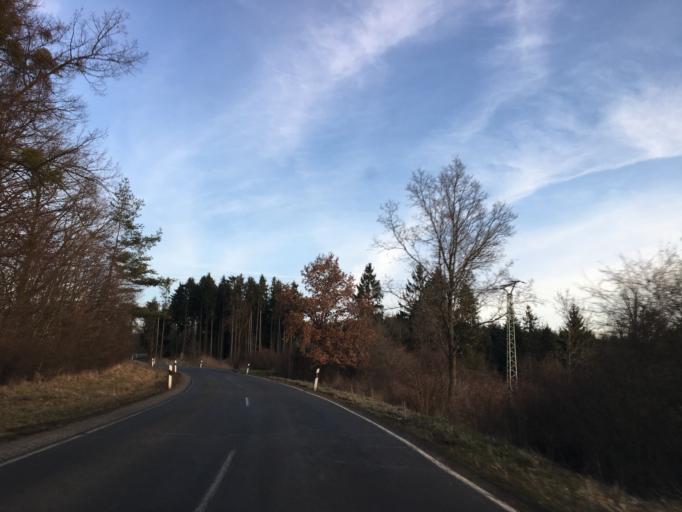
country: DE
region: Hesse
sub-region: Regierungsbezirk Giessen
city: Lauterbach
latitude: 50.6318
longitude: 9.3525
